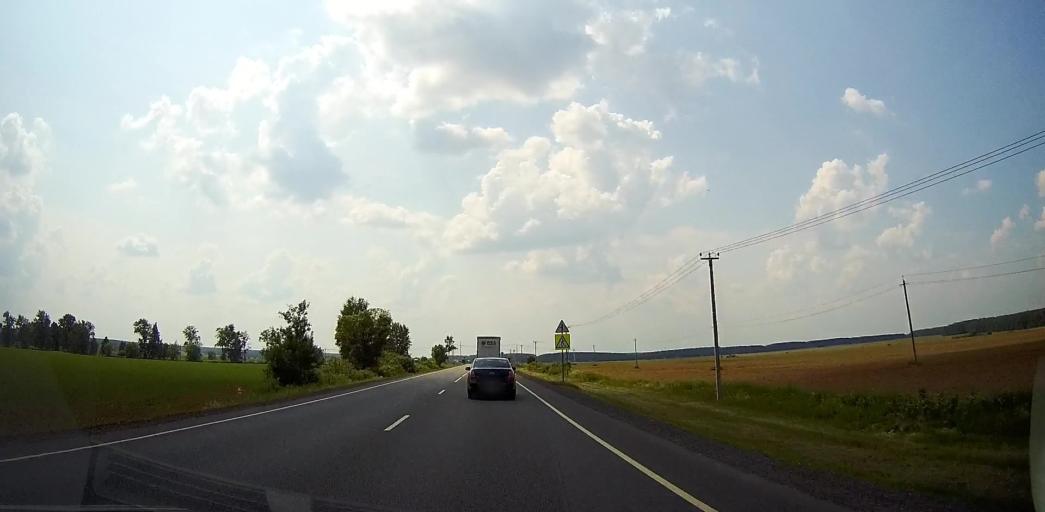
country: RU
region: Moskovskaya
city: Malino
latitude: 55.1330
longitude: 38.2574
